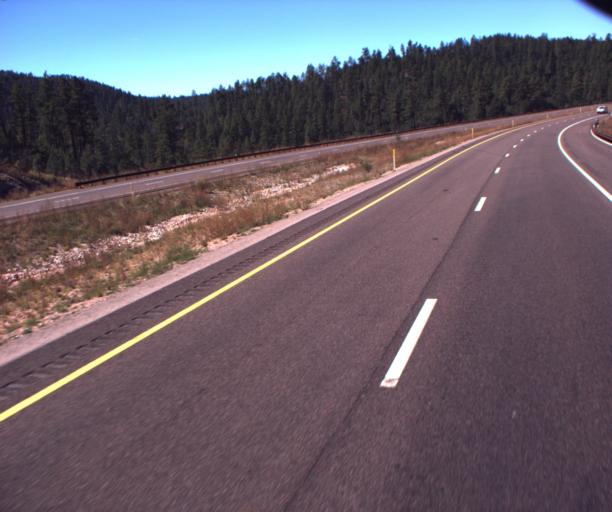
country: US
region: Arizona
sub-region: Gila County
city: Star Valley
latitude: 34.3244
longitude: -111.0827
